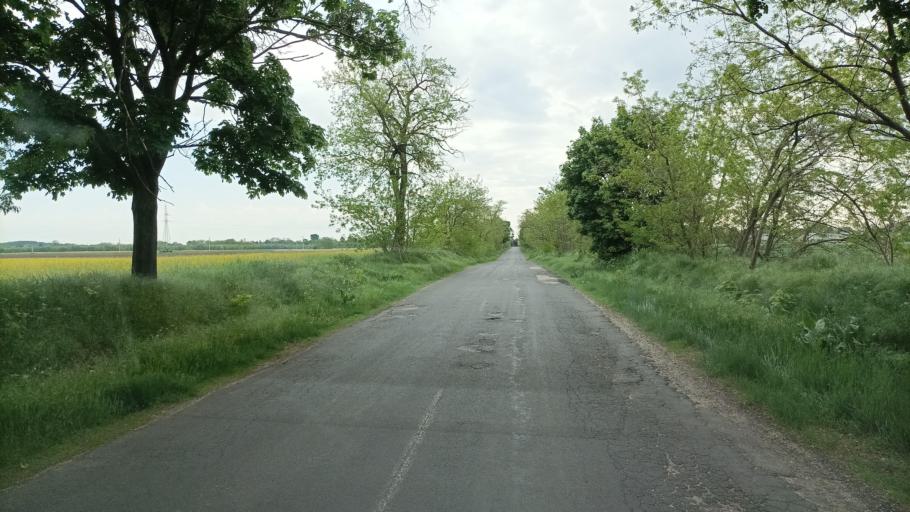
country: HU
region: Pest
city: Nyaregyhaza
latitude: 47.2693
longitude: 19.5176
